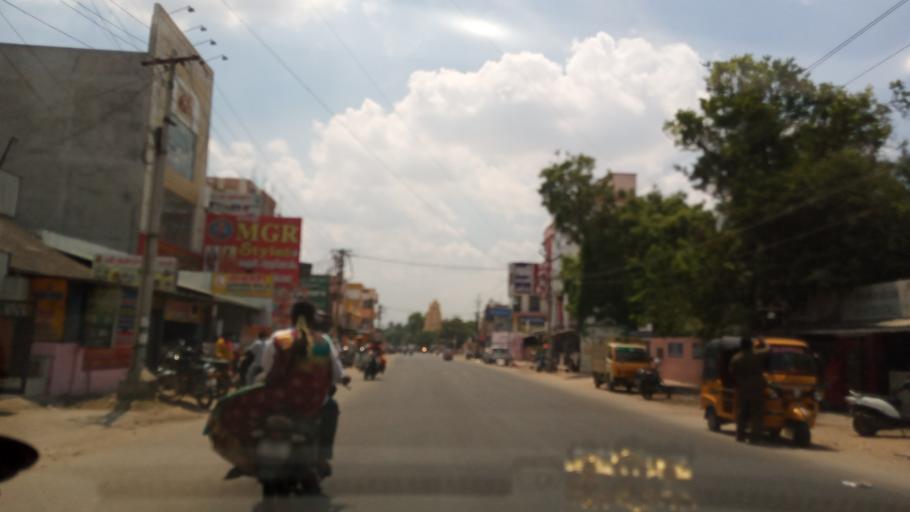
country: IN
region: Tamil Nadu
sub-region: Vellore
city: Walajapet
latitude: 12.9255
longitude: 79.3620
